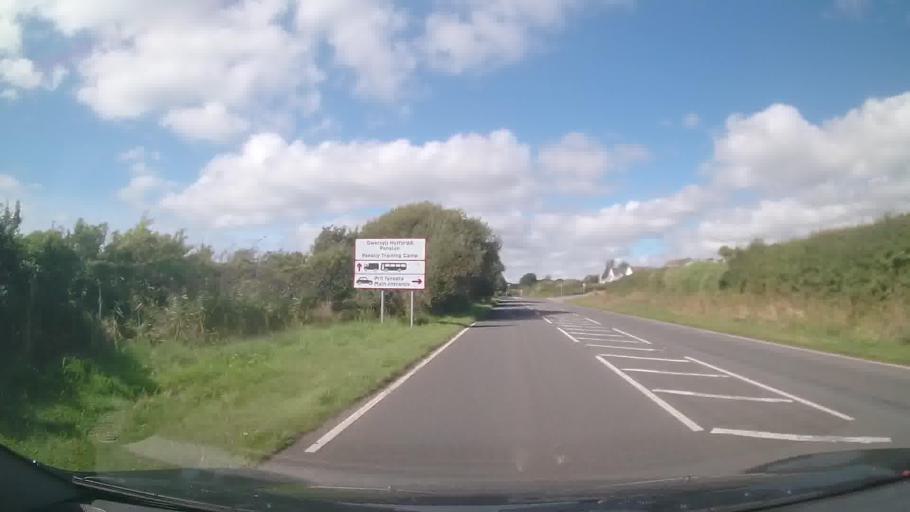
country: GB
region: Wales
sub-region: Pembrokeshire
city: Penally
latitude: 51.6567
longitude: -4.7293
